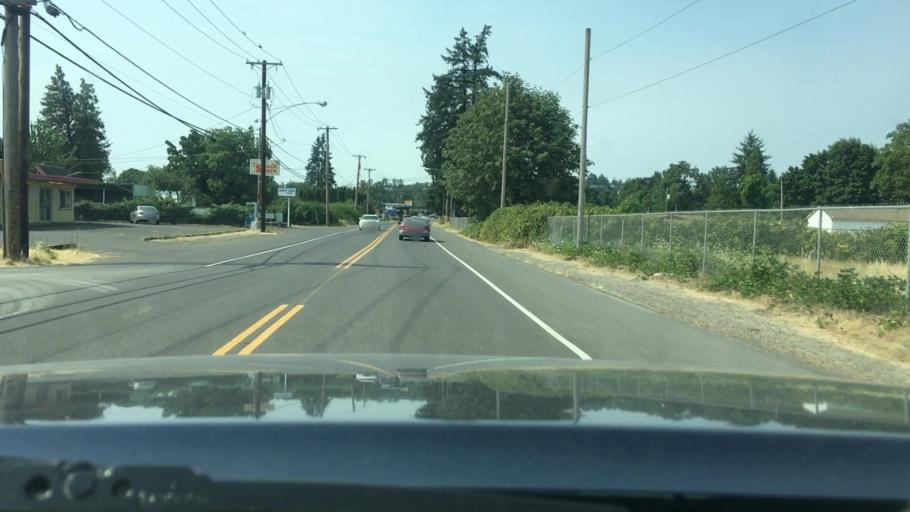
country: US
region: Oregon
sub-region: Lane County
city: Springfield
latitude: 44.0388
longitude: -123.0280
